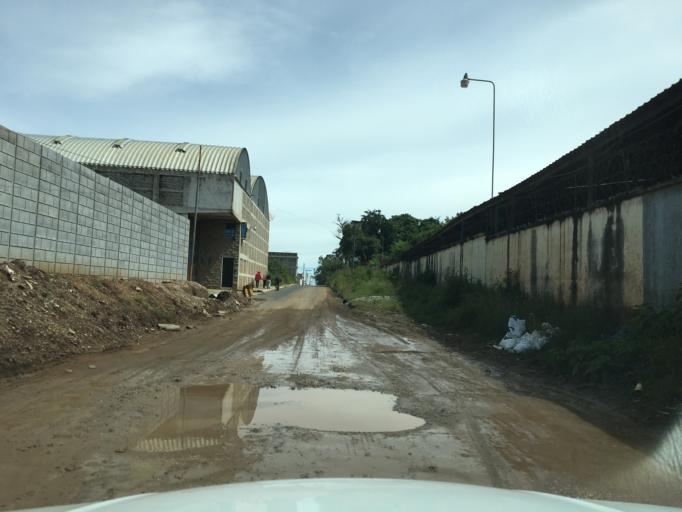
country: GT
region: Guatemala
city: Mixco
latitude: 14.6548
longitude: -90.5635
